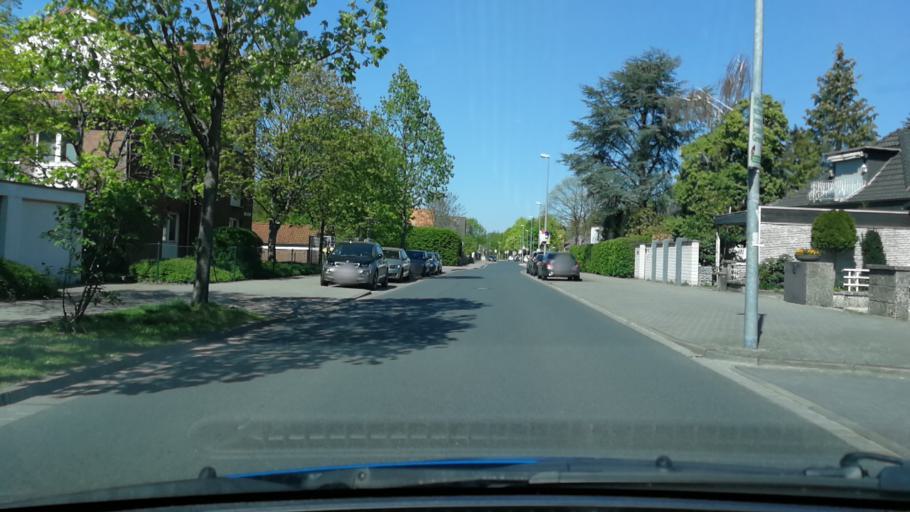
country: DE
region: Lower Saxony
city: Laatzen
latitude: 52.3481
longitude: 9.8210
